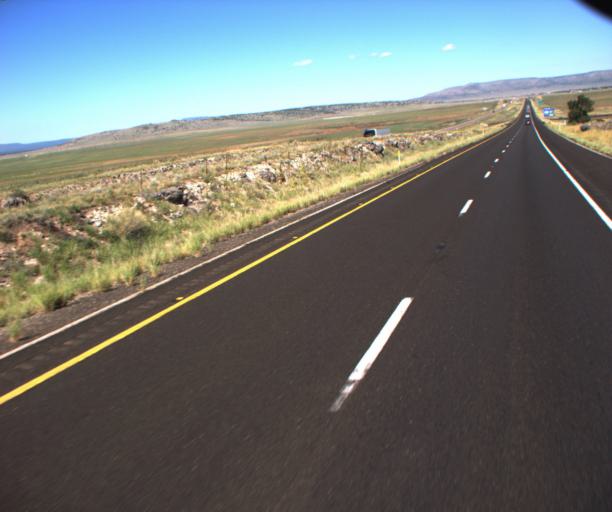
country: US
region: Arizona
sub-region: Yavapai County
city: Paulden
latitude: 35.2956
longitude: -112.8298
